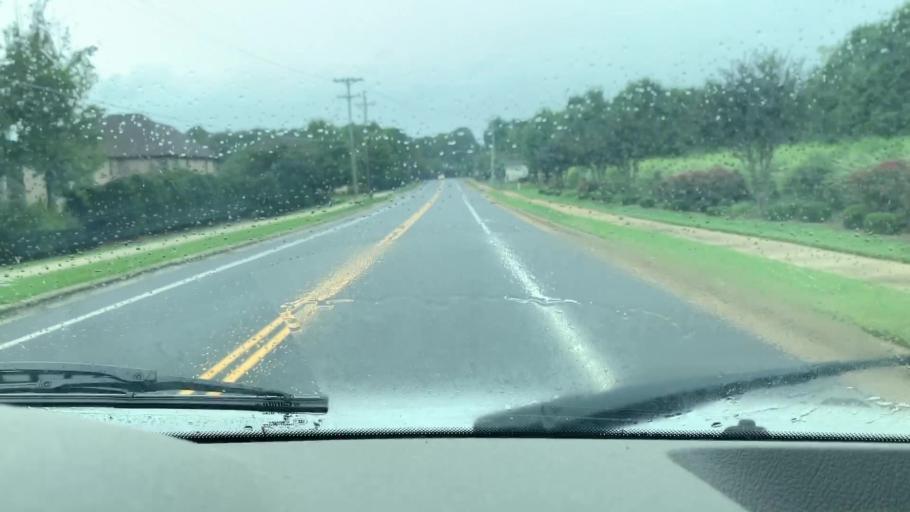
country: US
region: North Carolina
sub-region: Mecklenburg County
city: Cornelius
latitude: 35.4849
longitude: -80.8976
